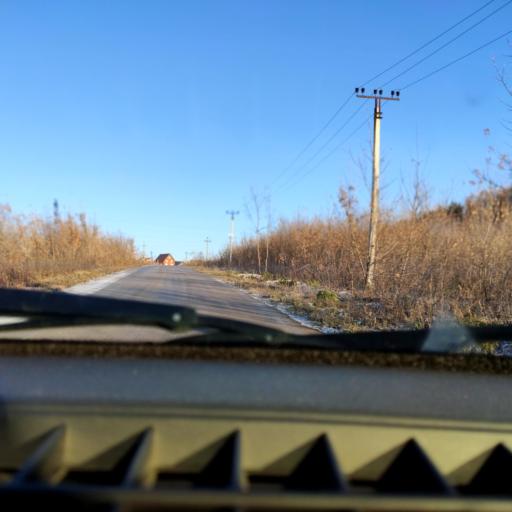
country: RU
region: Bashkortostan
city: Avdon
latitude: 54.6532
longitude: 55.7515
